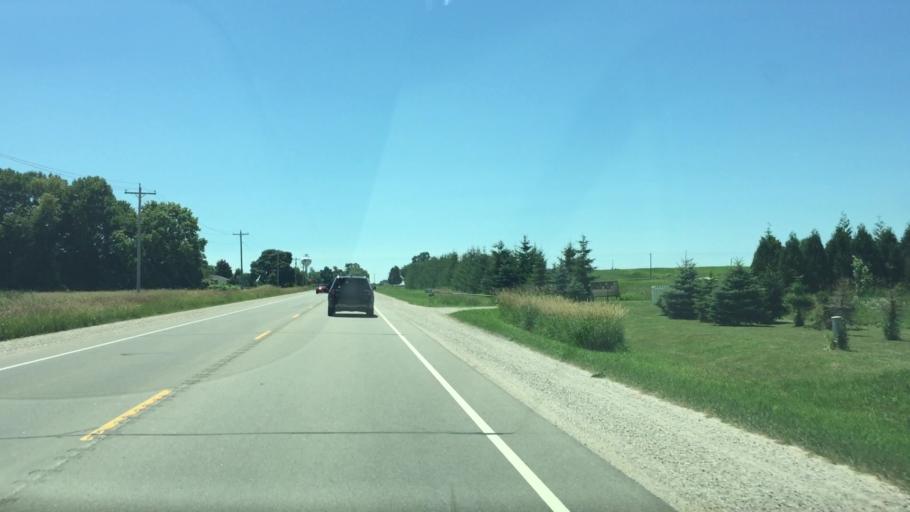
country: US
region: Wisconsin
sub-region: Calumet County
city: New Holstein
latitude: 43.9672
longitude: -88.1124
